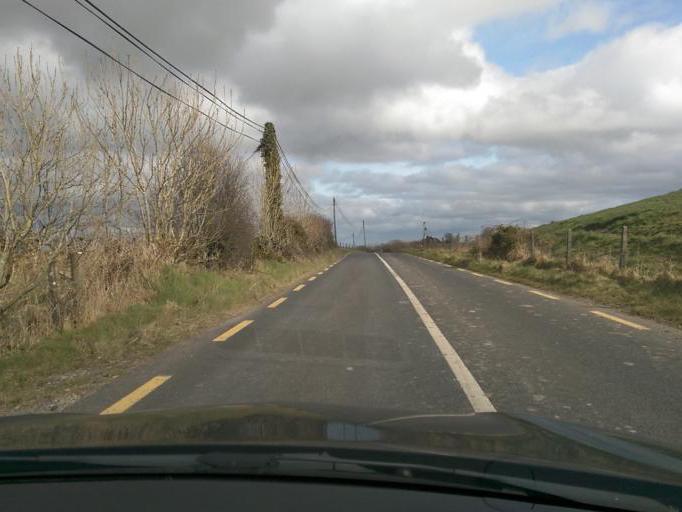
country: IE
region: Connaught
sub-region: County Galway
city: Ballinasloe
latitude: 53.3261
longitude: -8.4165
